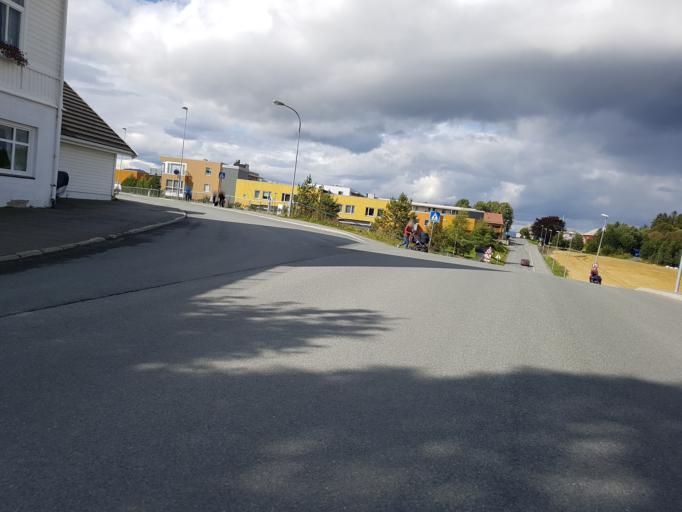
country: NO
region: Sor-Trondelag
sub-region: Trondheim
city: Trondheim
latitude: 63.4128
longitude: 10.4748
